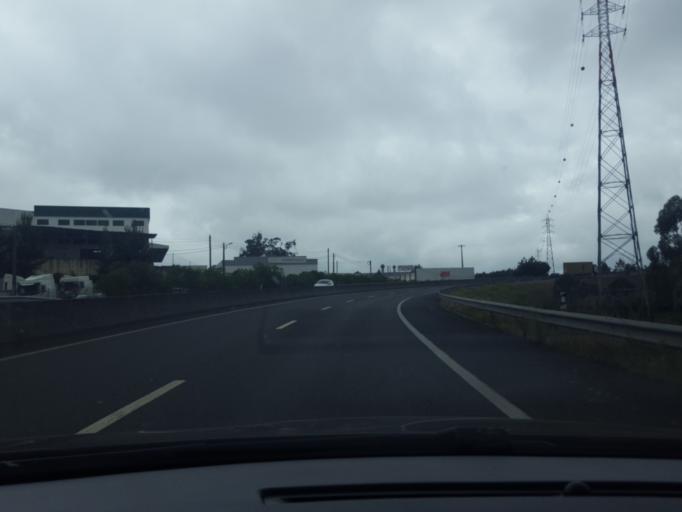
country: PT
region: Leiria
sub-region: Leiria
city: Leiria
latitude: 39.7621
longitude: -8.7775
